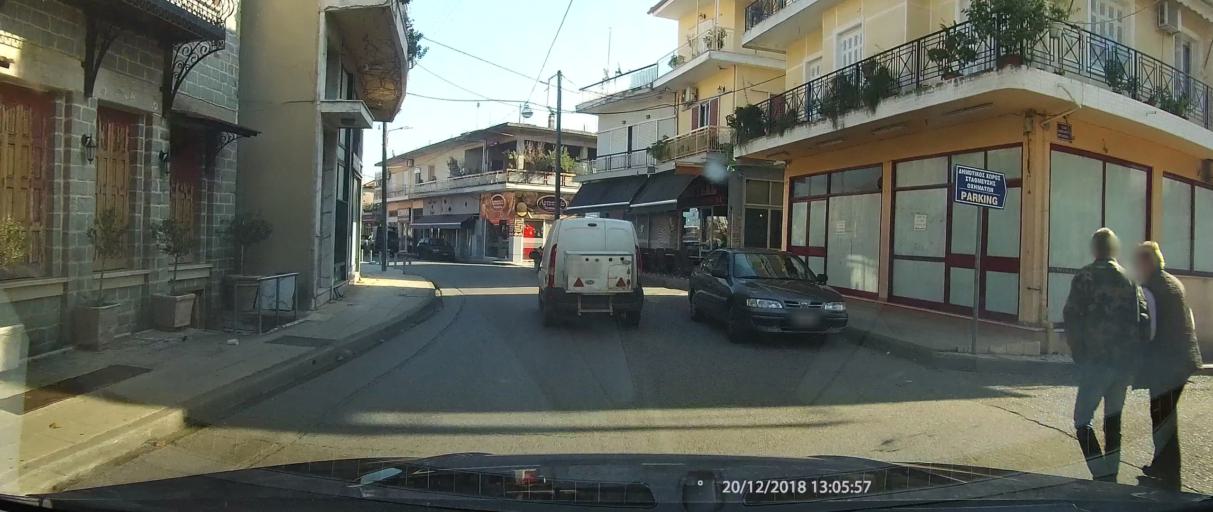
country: GR
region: West Greece
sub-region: Nomos Aitolias kai Akarnanias
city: Panaitolion
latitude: 38.5825
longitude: 21.4457
